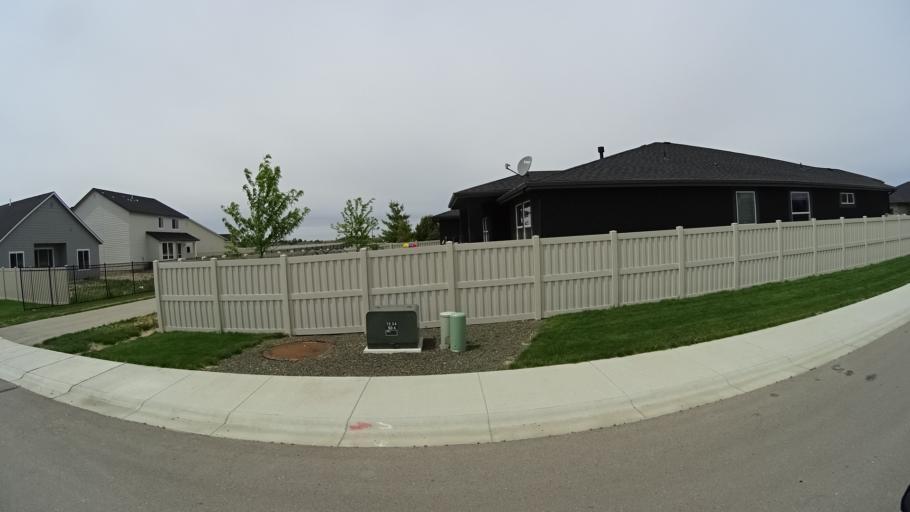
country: US
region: Idaho
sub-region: Ada County
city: Meridian
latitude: 43.5650
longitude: -116.3511
